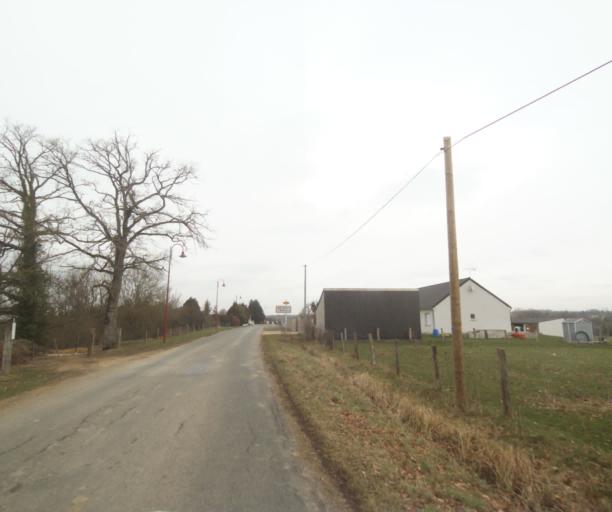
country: FR
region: Champagne-Ardenne
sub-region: Departement de la Marne
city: Pargny-sur-Saulx
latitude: 48.7454
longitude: 4.8422
